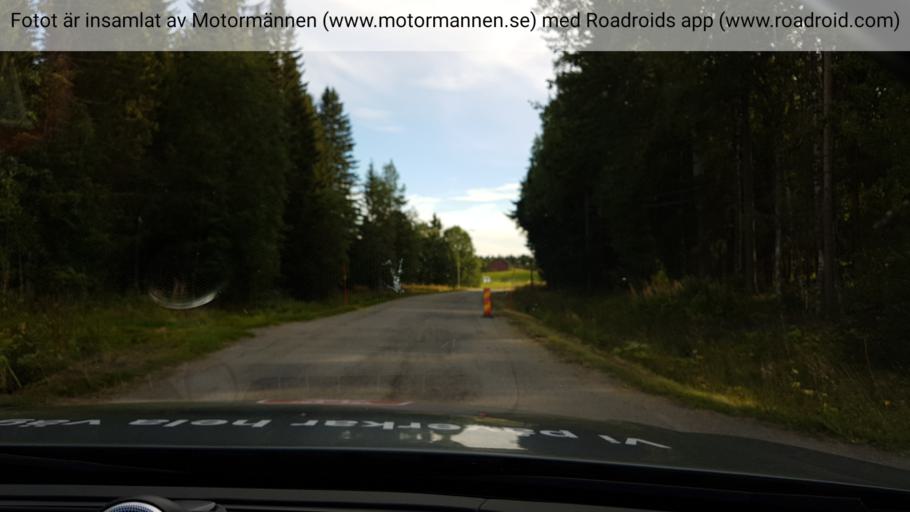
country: SE
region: Jaemtland
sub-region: Stroemsunds Kommun
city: Stroemsund
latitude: 64.0744
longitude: 15.8260
